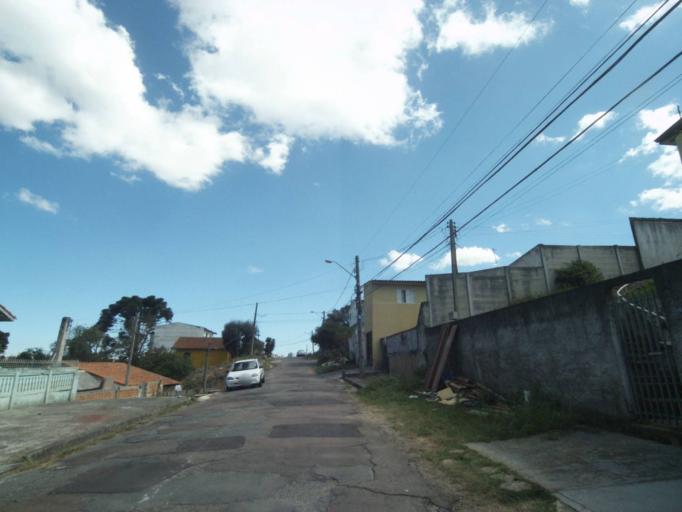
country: BR
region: Parana
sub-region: Curitiba
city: Curitiba
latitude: -25.3824
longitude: -49.2413
